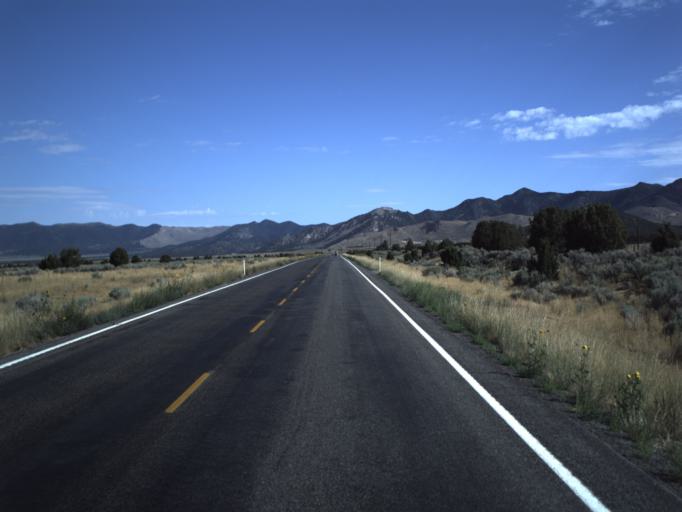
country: US
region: Utah
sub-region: Juab County
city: Mona
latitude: 39.8676
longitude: -112.1380
